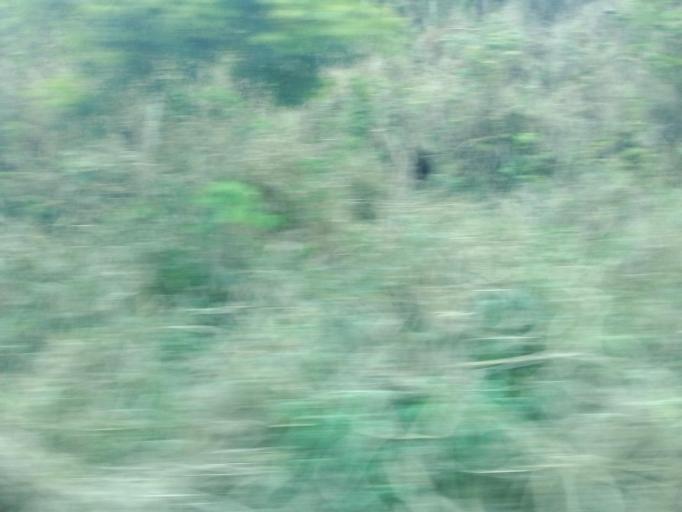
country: BR
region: Minas Gerais
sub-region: Ipaba
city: Ipaba
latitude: -19.4636
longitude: -42.4542
